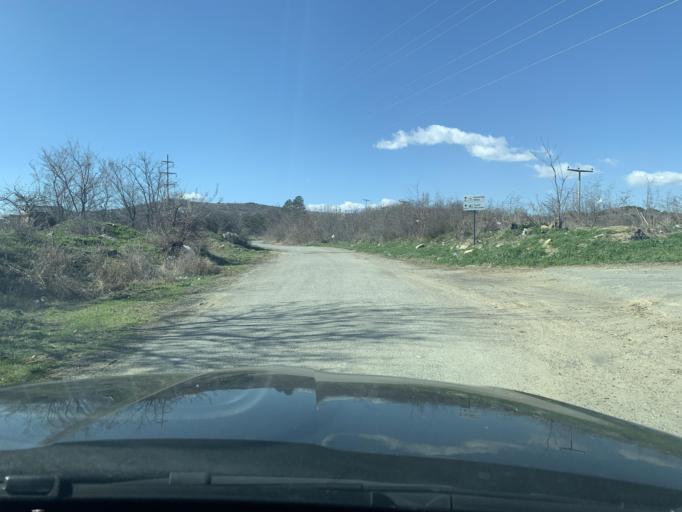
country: MK
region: Demir Kapija
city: Demir Kapija
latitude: 41.4091
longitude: 22.2329
